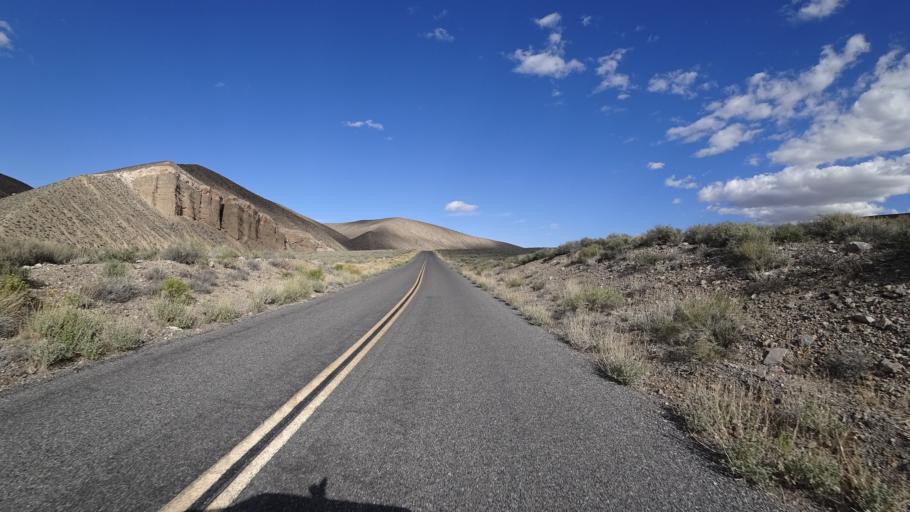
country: US
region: Nevada
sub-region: Nye County
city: Beatty
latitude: 36.3965
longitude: -117.1631
